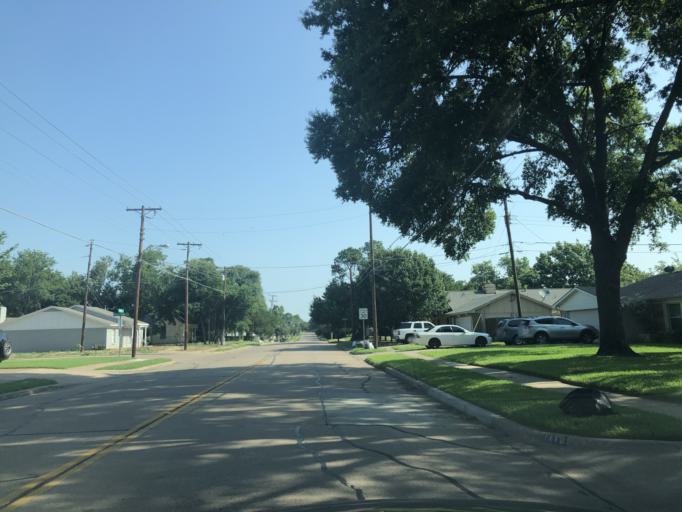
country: US
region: Texas
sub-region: Dallas County
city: Irving
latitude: 32.8035
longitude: -96.9708
